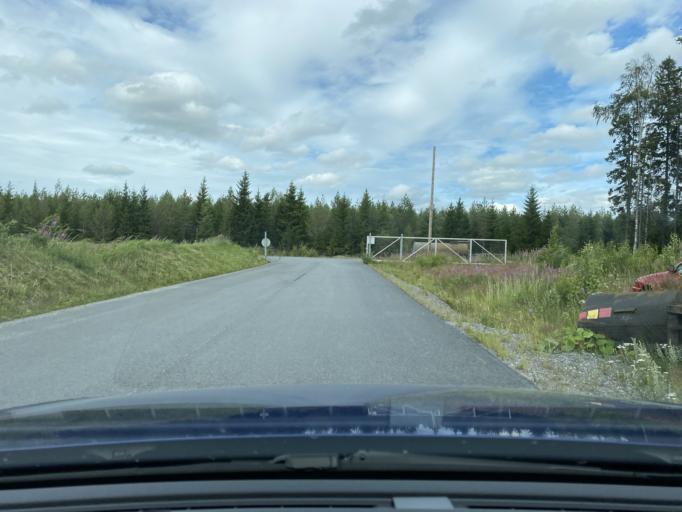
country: FI
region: Southern Ostrobothnia
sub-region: Seinaejoki
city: Jurva
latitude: 62.6239
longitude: 22.0328
